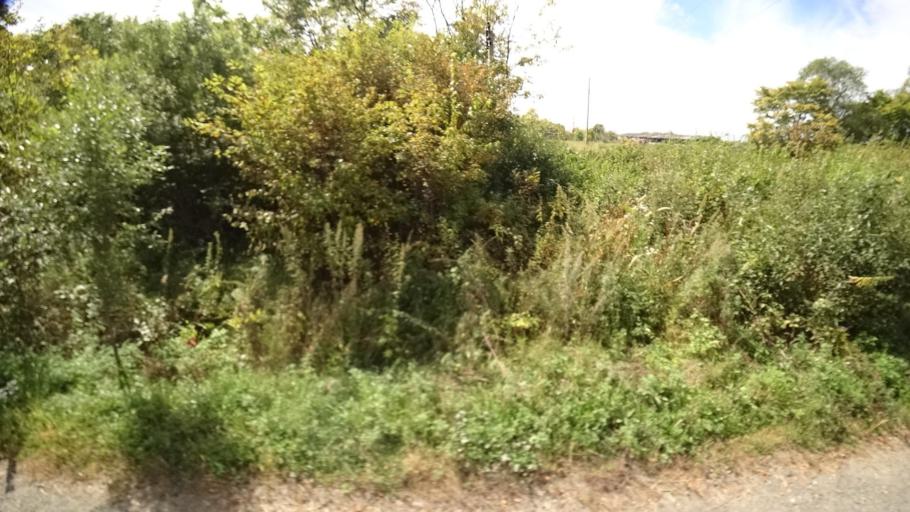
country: RU
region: Primorskiy
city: Yakovlevka
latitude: 44.6427
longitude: 133.5956
